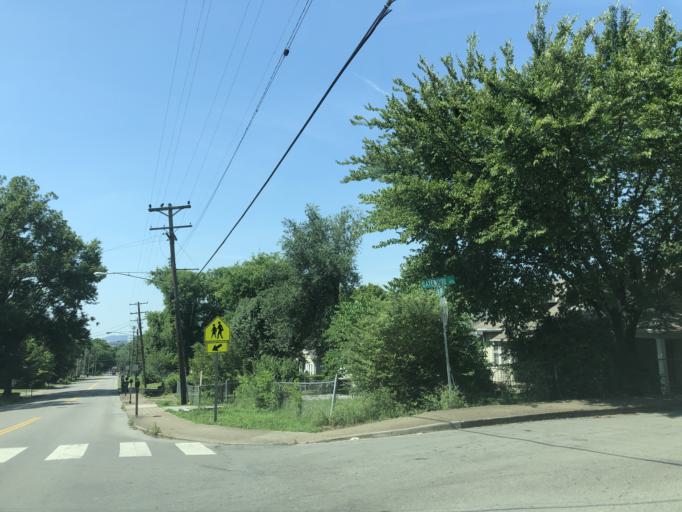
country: US
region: Tennessee
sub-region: Davidson County
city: Nashville
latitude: 36.2000
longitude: -86.7666
